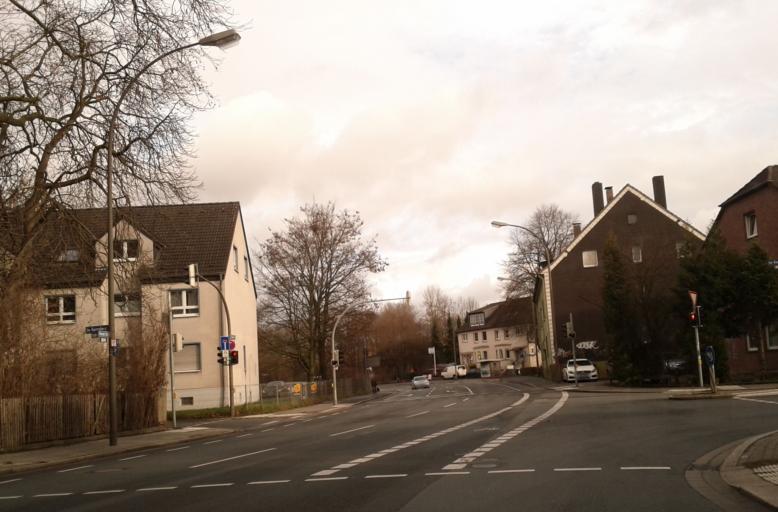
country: DE
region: North Rhine-Westphalia
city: Lanstrop
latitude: 51.5568
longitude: 7.5105
